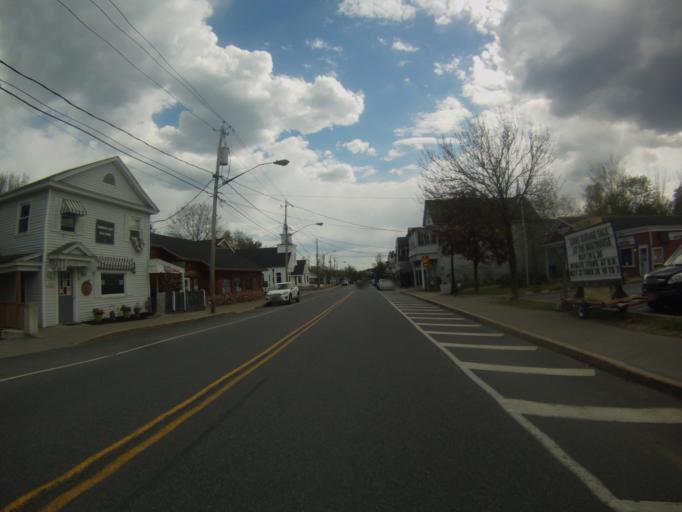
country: US
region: New York
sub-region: Essex County
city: Ticonderoga
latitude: 43.8375
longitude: -73.7615
